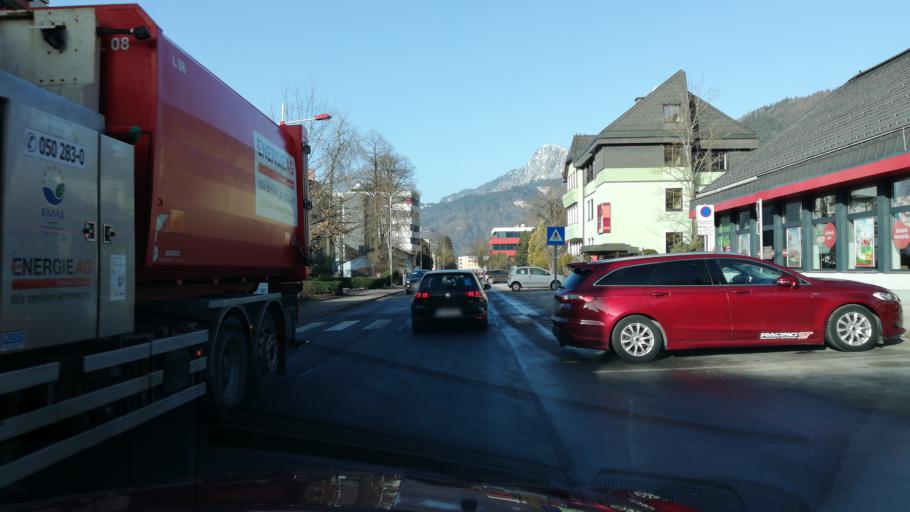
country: AT
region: Styria
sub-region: Politischer Bezirk Liezen
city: Liezen
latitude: 47.5694
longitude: 14.2390
